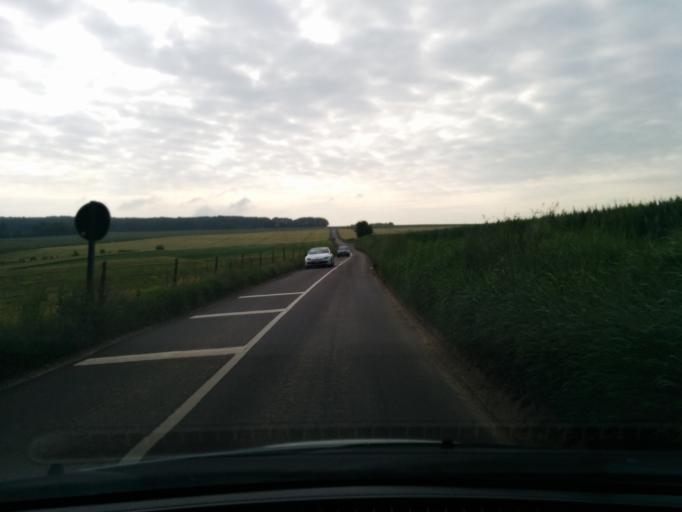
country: FR
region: Ile-de-France
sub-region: Departement des Yvelines
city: Follainville-Dennemont
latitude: 49.0867
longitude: 1.6778
